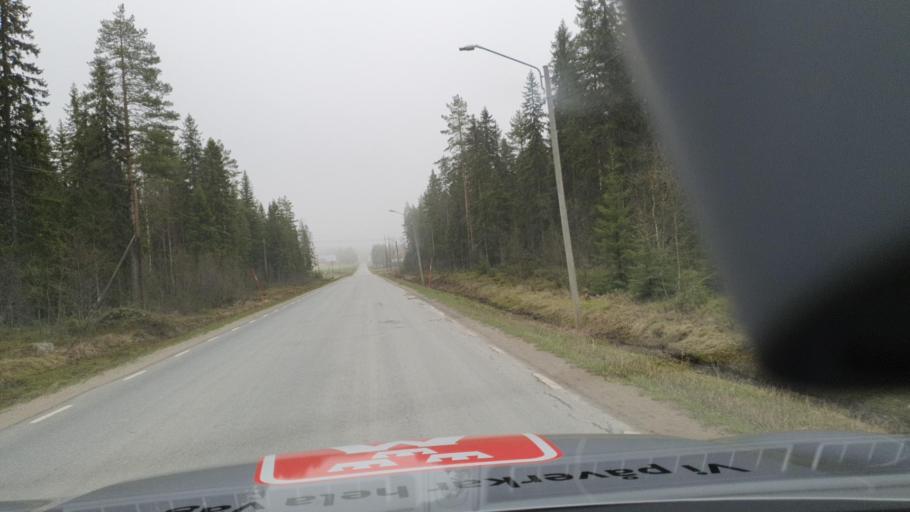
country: SE
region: Vaesternorrland
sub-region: OErnskoeldsviks Kommun
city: Husum
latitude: 63.5883
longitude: 19.0189
